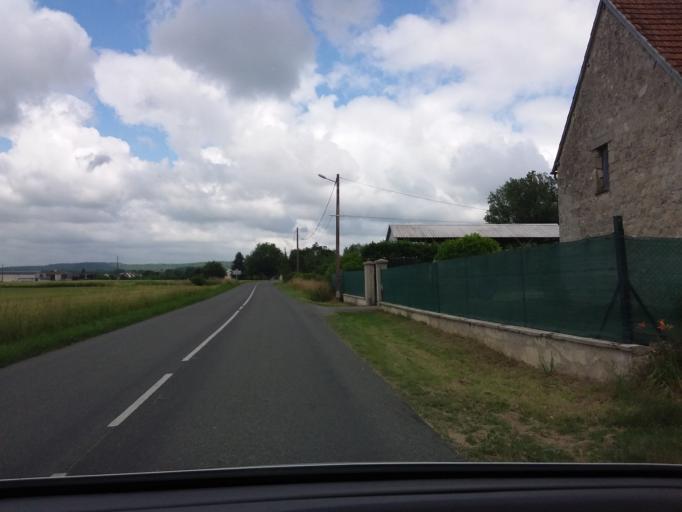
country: FR
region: Picardie
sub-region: Departement de l'Aisne
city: Vailly-sur-Aisne
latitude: 49.4065
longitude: 3.5331
